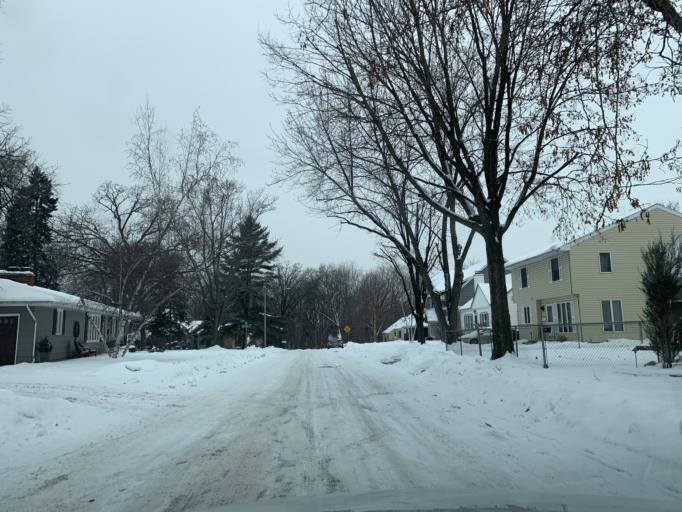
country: US
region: Minnesota
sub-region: Hennepin County
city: Saint Louis Park
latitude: 44.9432
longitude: -93.3307
